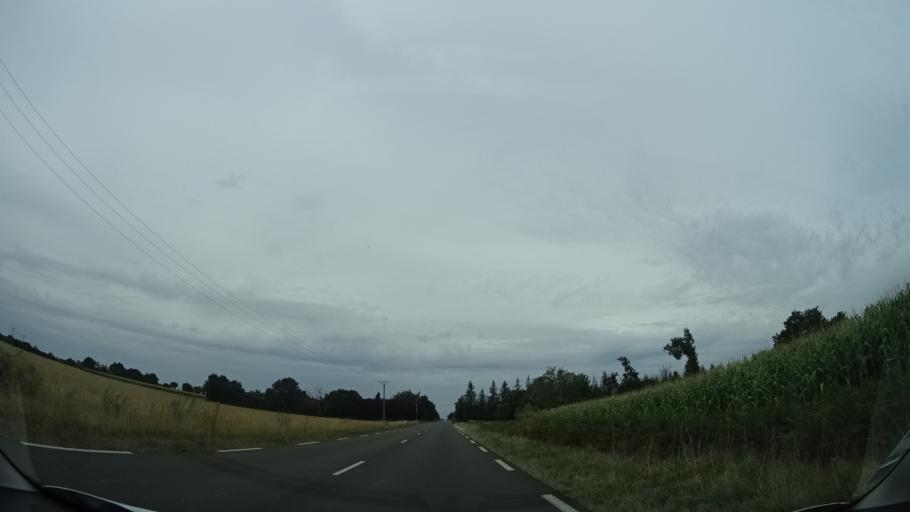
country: FR
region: Pays de la Loire
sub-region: Departement de la Mayenne
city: Meslay-du-Maine
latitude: 47.9622
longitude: -0.5755
